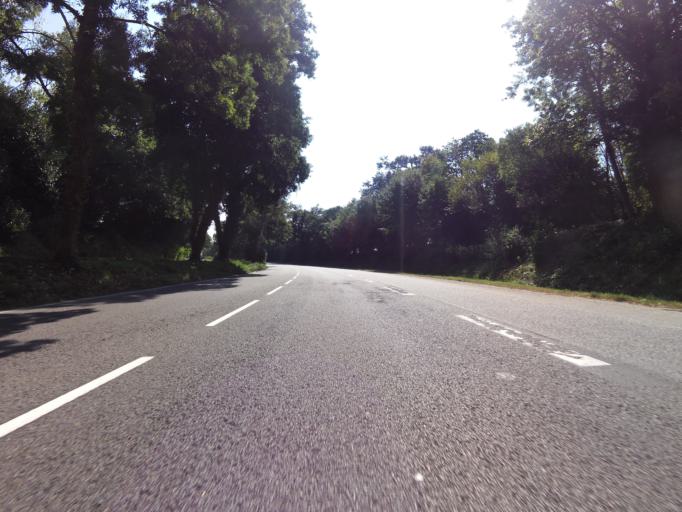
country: FR
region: Brittany
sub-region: Departement du Finistere
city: Quimper
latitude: 47.9802
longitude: -4.1081
